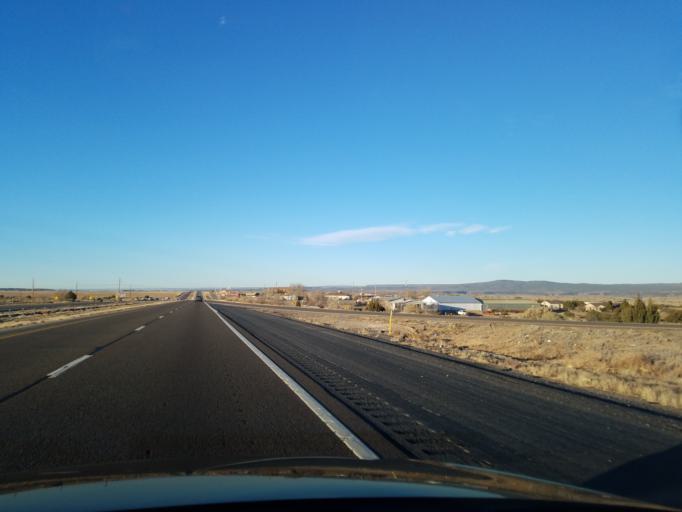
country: US
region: New Mexico
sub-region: Sandoval County
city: Santo Domingo Pueblo
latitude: 35.4584
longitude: -106.3337
